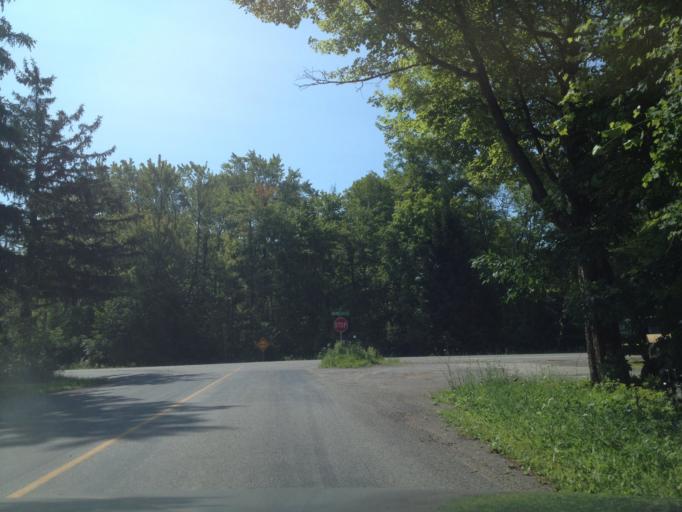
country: CA
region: Ontario
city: Norfolk County
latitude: 42.8135
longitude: -80.3755
